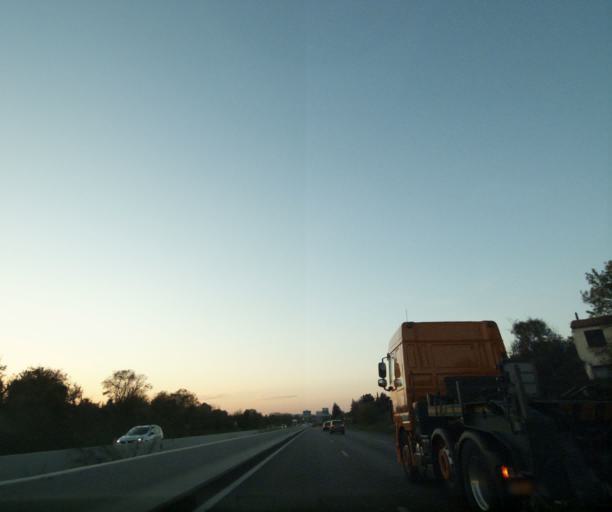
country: FR
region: Provence-Alpes-Cote d'Azur
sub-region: Departement des Bouches-du-Rhone
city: Arles
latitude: 43.6591
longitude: 4.6451
